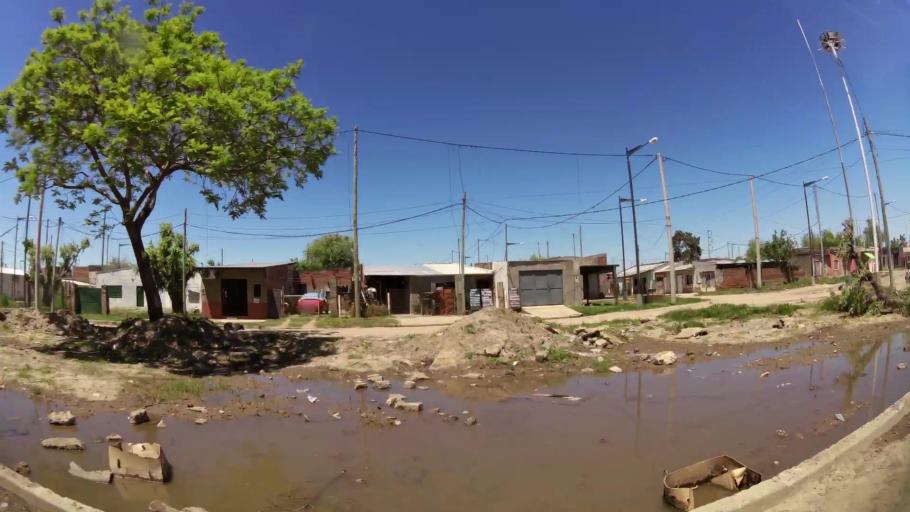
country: AR
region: Santa Fe
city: Santa Fe de la Vera Cruz
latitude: -31.6216
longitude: -60.7201
